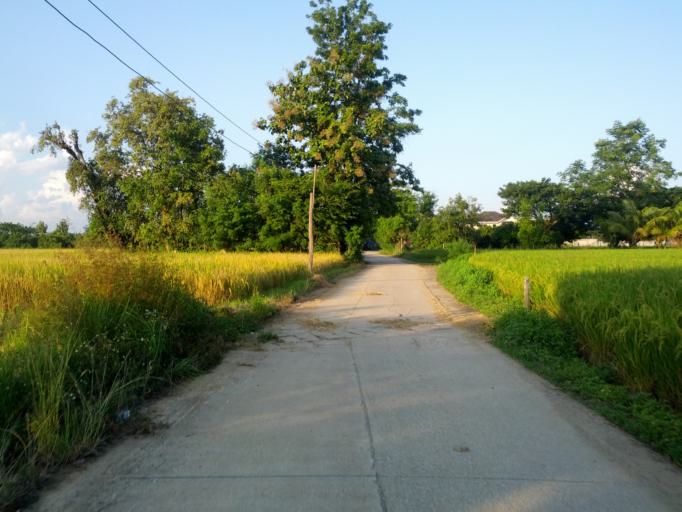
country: TH
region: Chiang Mai
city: San Kamphaeng
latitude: 18.7473
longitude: 99.0815
